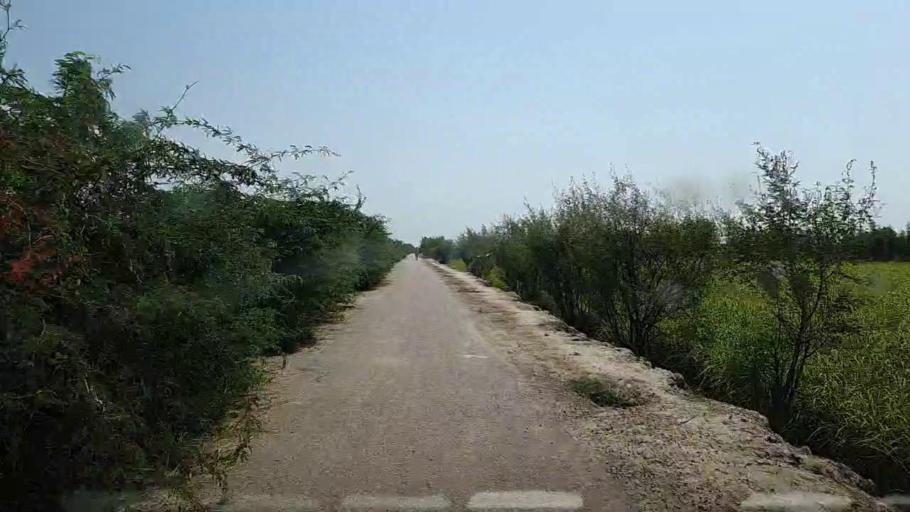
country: PK
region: Sindh
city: Mirpur Batoro
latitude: 24.6168
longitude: 68.4522
